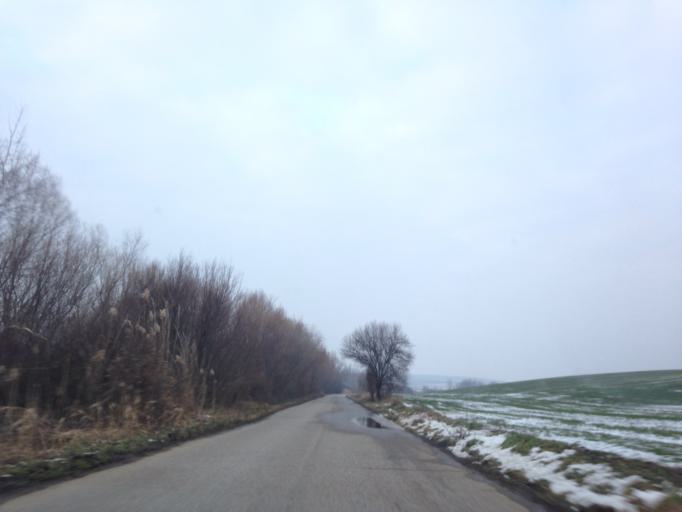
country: SK
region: Nitriansky
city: Svodin
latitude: 48.0450
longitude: 18.3702
